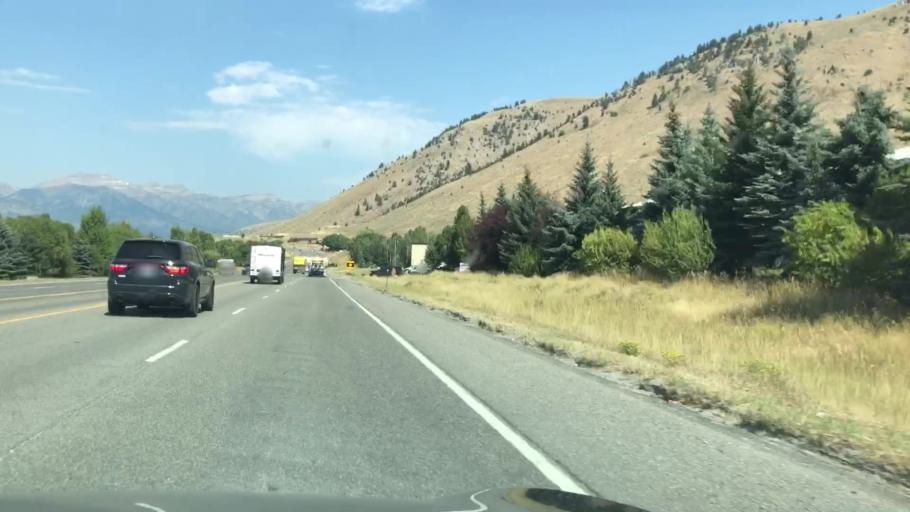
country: US
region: Wyoming
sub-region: Teton County
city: South Park
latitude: 43.4221
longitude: -110.7763
